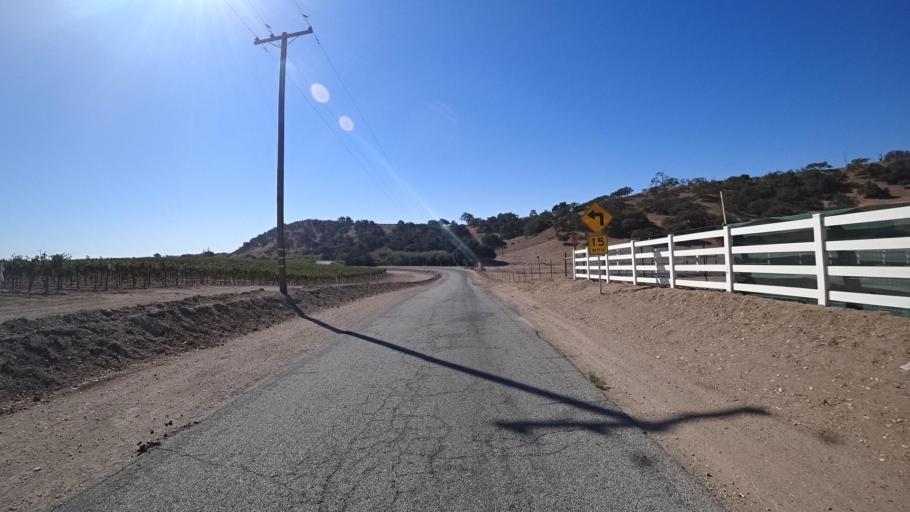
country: US
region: California
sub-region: Monterey County
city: King City
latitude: 36.1412
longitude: -121.1011
